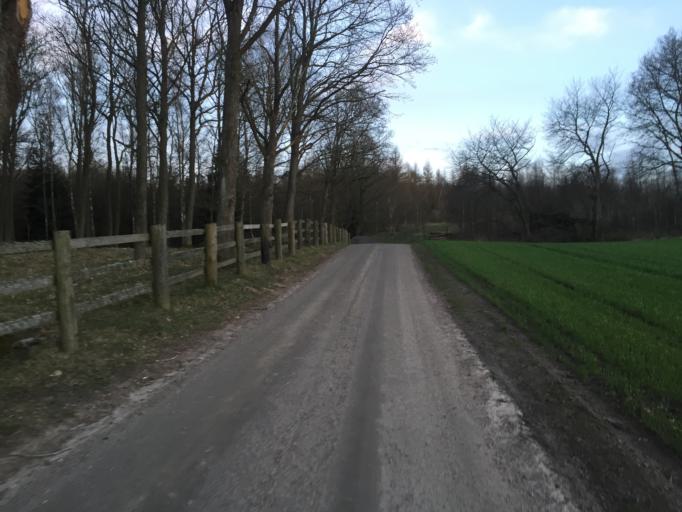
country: SE
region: Skane
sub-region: Lunds Kommun
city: Veberod
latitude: 55.6140
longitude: 13.5098
